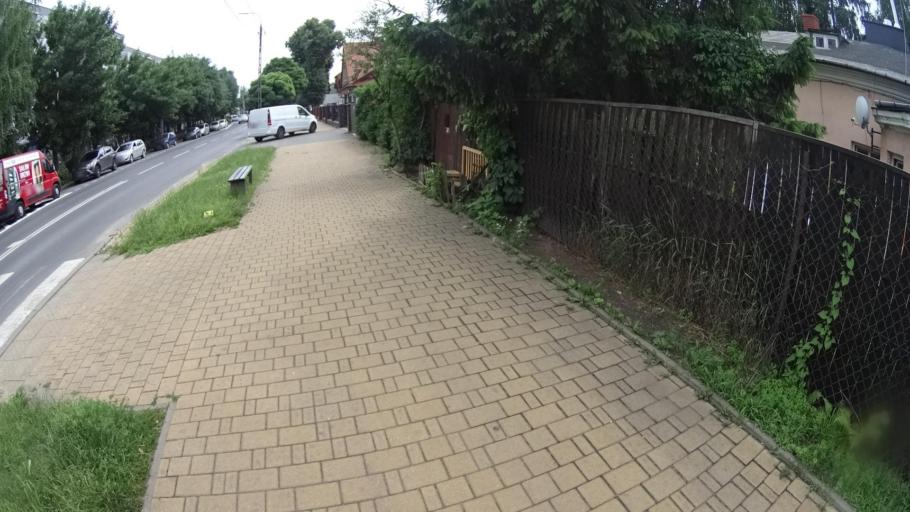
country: PL
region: Masovian Voivodeship
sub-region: Powiat grojecki
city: Grojec
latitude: 51.8634
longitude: 20.8673
